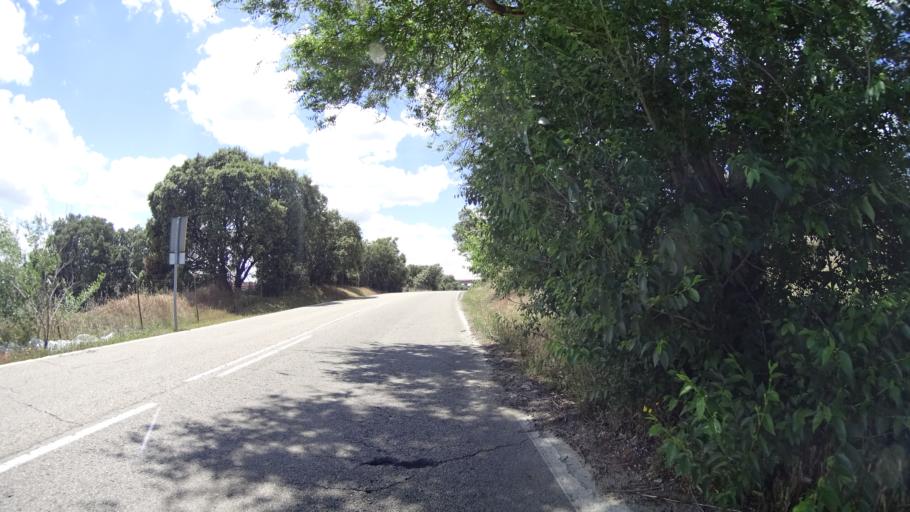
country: ES
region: Madrid
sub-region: Provincia de Madrid
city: Villanueva del Pardillo
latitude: 40.4614
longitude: -3.9457
